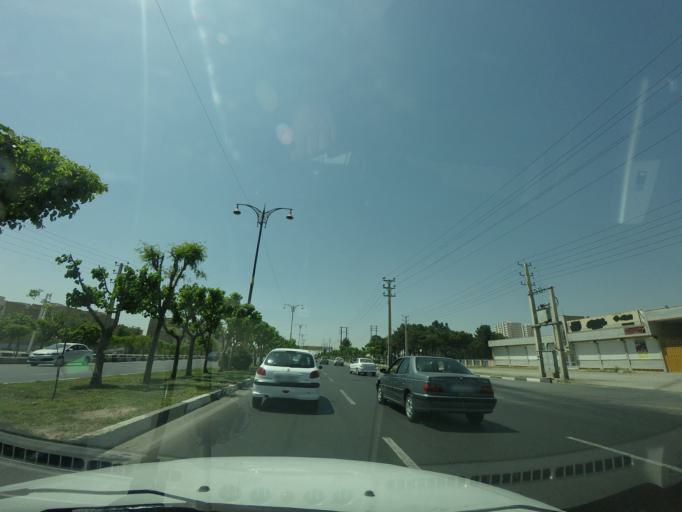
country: IR
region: Tehran
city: Eslamshahr
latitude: 35.5427
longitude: 51.2158
